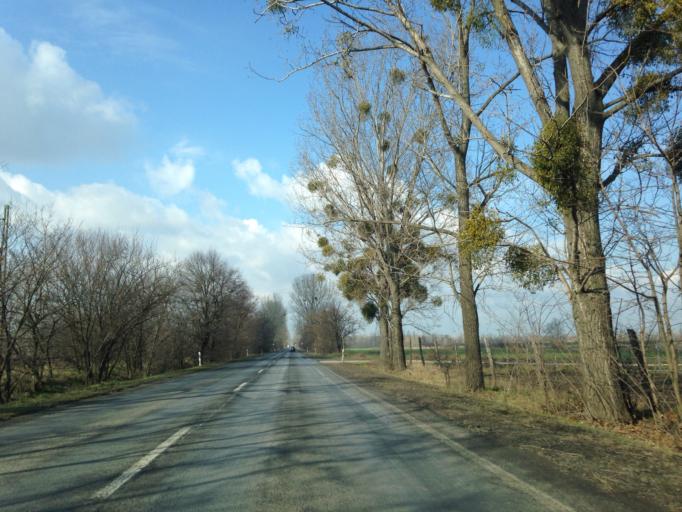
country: HU
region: Komarom-Esztergom
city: Almasfuzito
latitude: 47.7128
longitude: 18.2854
